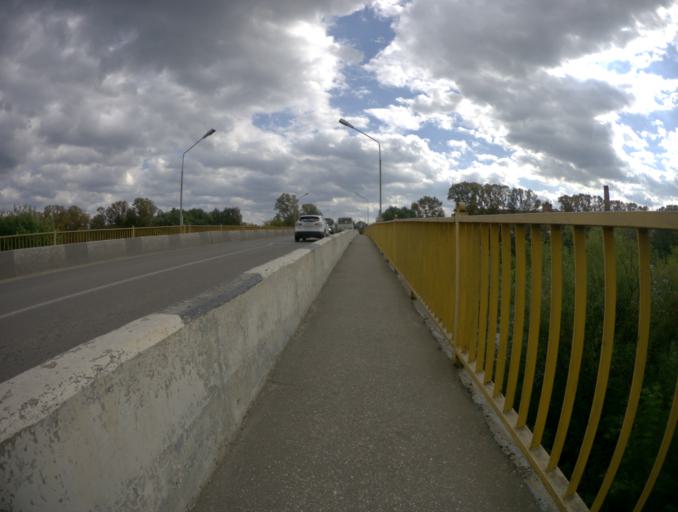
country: RU
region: Vladimir
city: Sobinka
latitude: 55.9973
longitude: 40.0163
